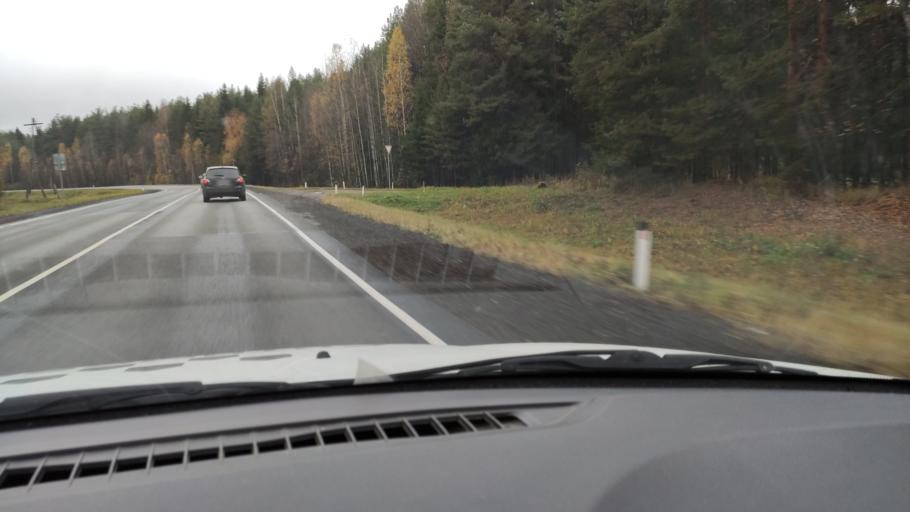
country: RU
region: Kirov
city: Belaya Kholunitsa
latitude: 58.8728
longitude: 50.8507
